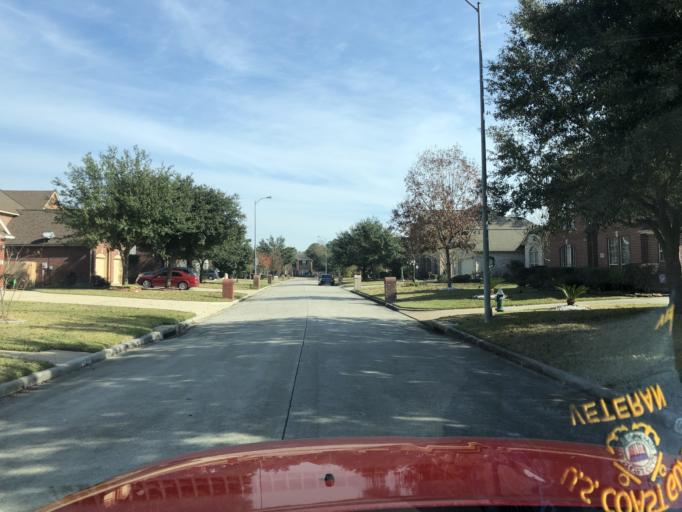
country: US
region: Texas
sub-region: Harris County
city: Tomball
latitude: 30.0267
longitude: -95.5589
